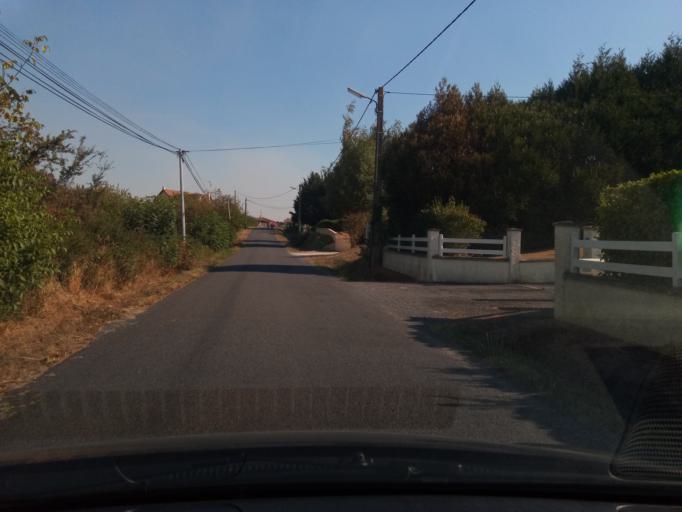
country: FR
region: Poitou-Charentes
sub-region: Departement de la Vienne
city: Montmorillon
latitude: 46.4170
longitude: 0.8726
